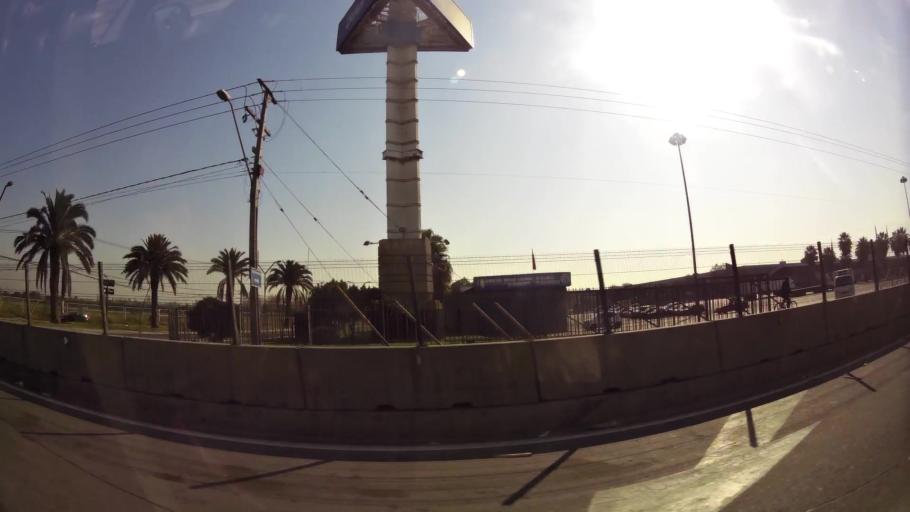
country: CL
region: Santiago Metropolitan
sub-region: Provincia de Santiago
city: Lo Prado
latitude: -33.5169
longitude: -70.7115
